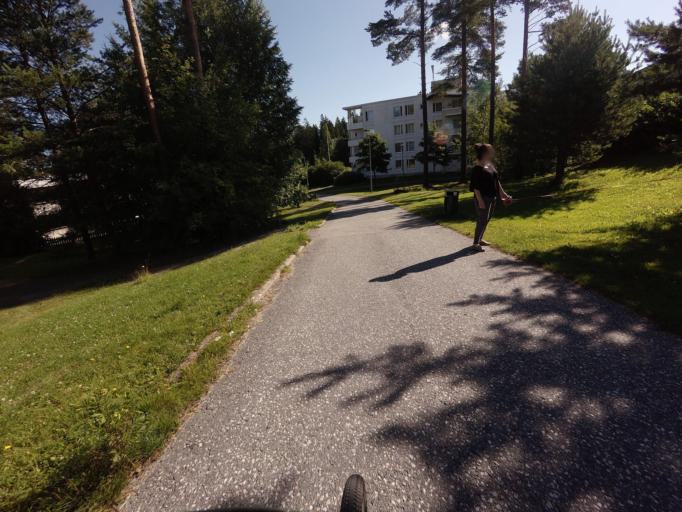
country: FI
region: Uusimaa
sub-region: Helsinki
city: Espoo
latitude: 60.1695
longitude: 24.6759
